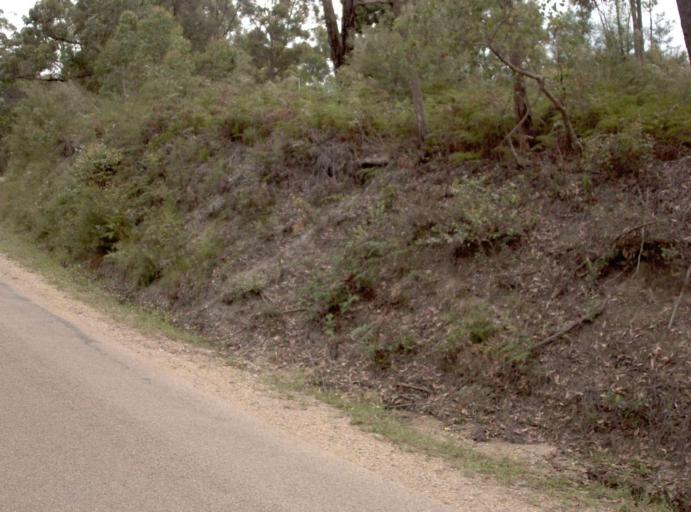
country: AU
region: Victoria
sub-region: East Gippsland
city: Bairnsdale
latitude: -37.7472
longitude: 147.5974
